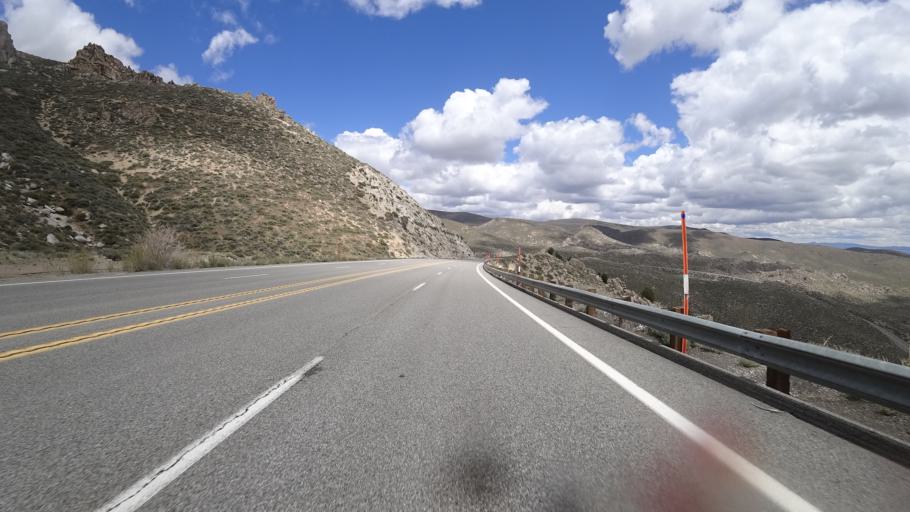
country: US
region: California
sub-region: Mono County
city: Bridgeport
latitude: 38.0778
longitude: -119.1703
